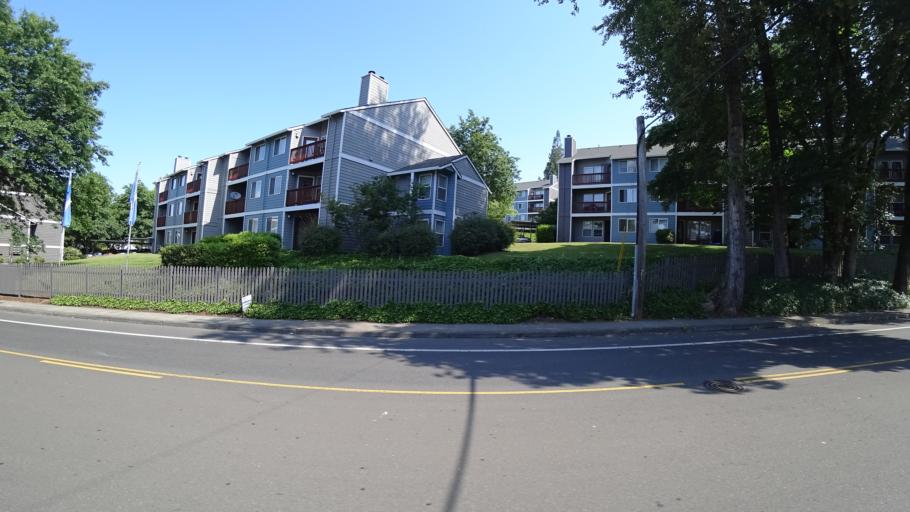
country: US
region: Oregon
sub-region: Clackamas County
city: Oatfield
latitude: 45.4479
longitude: -122.5941
